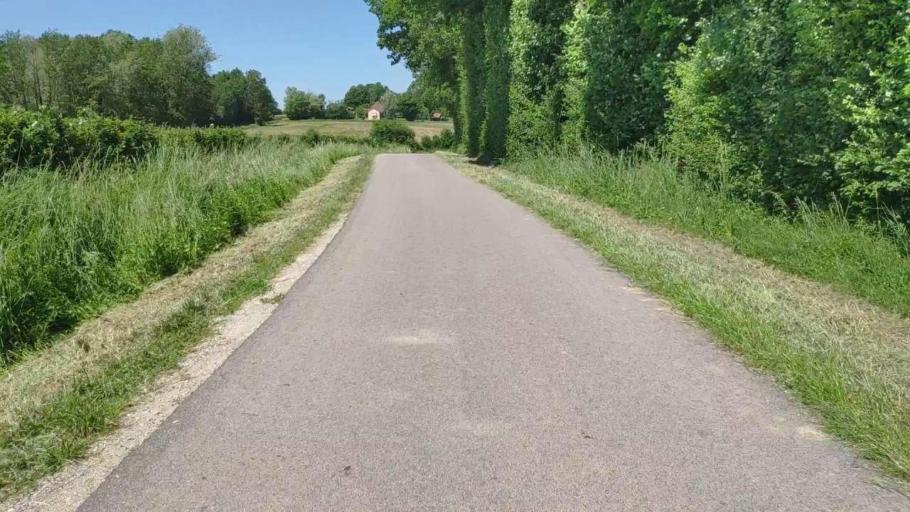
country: FR
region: Franche-Comte
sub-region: Departement du Jura
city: Bletterans
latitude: 46.7529
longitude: 5.3735
